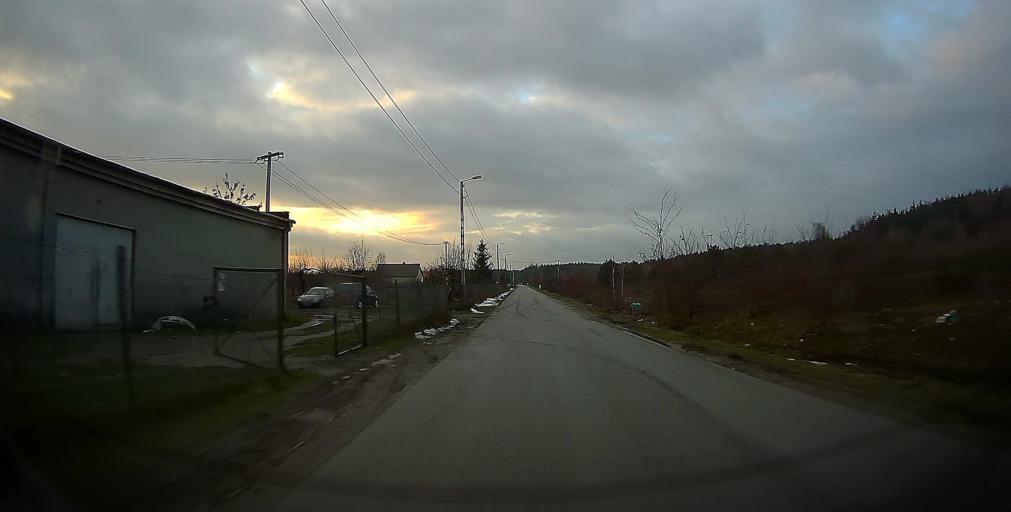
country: PL
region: Masovian Voivodeship
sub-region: Powiat radomski
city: Jedlinsk
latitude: 51.4584
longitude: 21.1112
